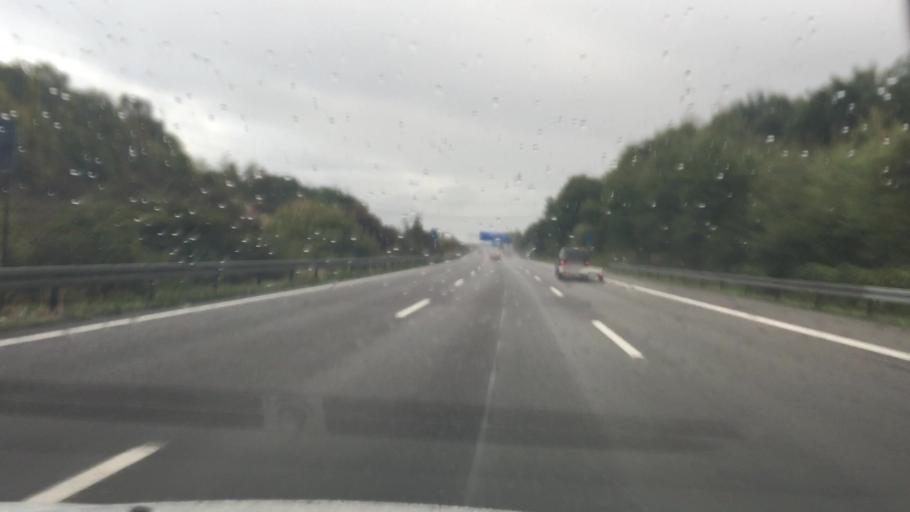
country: DE
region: Lower Saxony
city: Rennau
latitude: 52.2828
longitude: 10.9083
